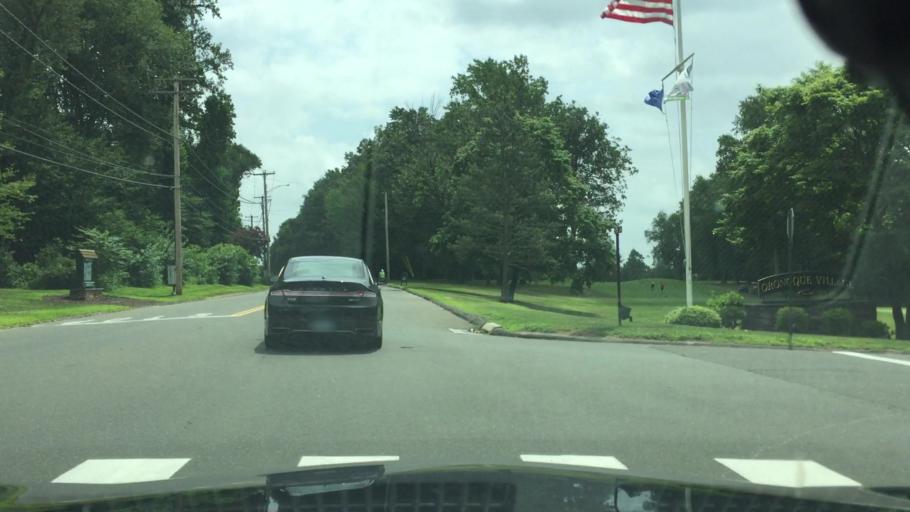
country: US
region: Connecticut
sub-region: New Haven County
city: City of Milford (balance)
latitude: 41.2503
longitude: -73.1103
